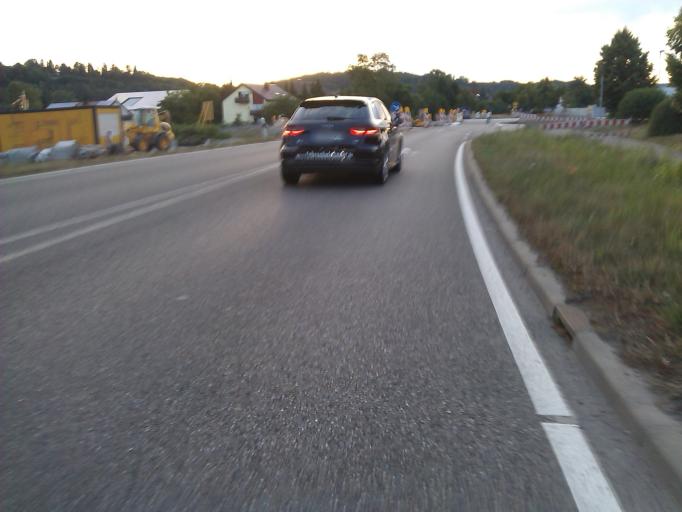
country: DE
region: Baden-Wuerttemberg
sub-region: Regierungsbezirk Stuttgart
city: Offenau
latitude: 49.2382
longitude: 9.1679
